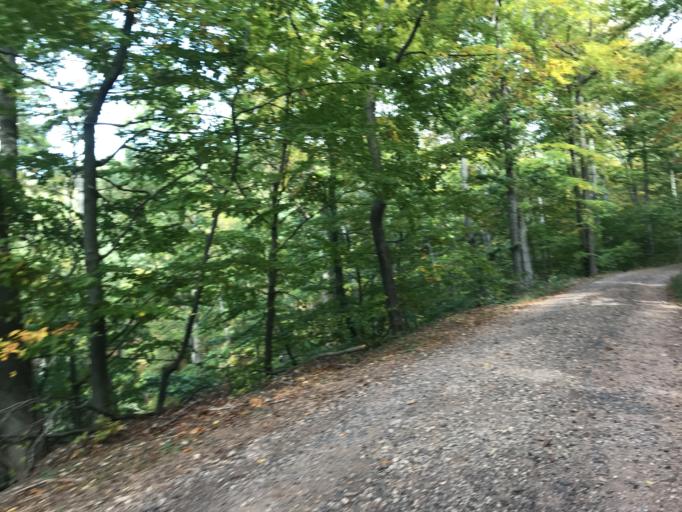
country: DE
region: Rheinland-Pfalz
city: Dannenfels
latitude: 49.6564
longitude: 7.9689
